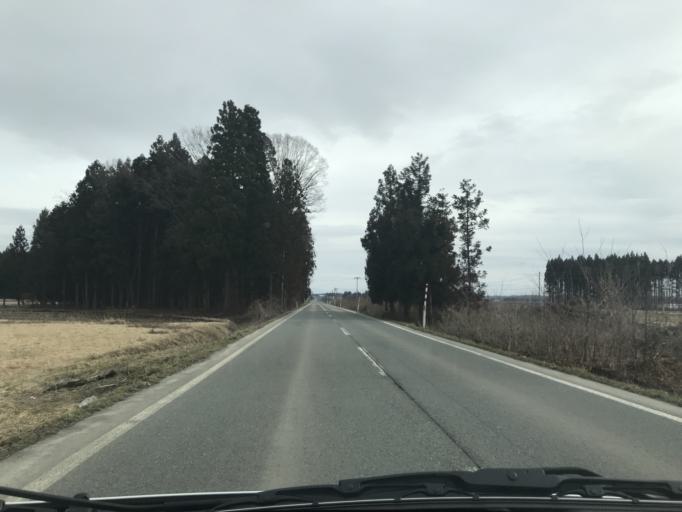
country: JP
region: Iwate
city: Kitakami
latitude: 39.3149
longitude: 141.0188
